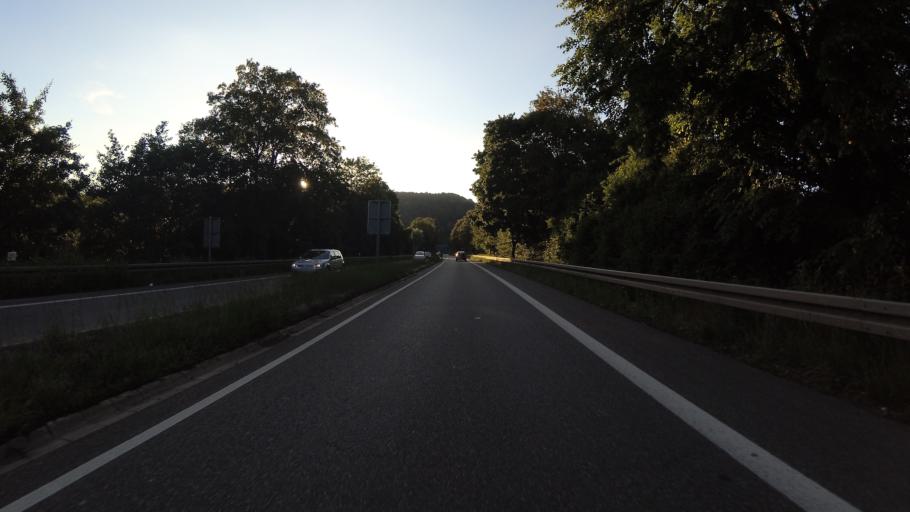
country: FR
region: Lorraine
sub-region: Departement de la Moselle
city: Alsting
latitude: 49.2003
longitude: 7.0254
